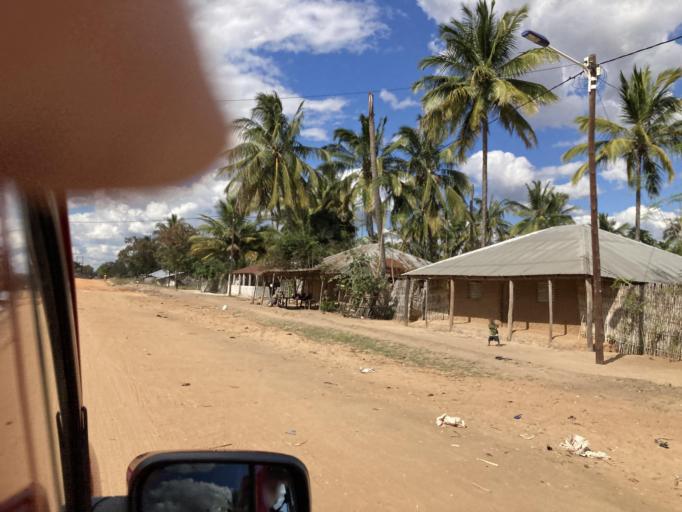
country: MZ
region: Cabo Delgado
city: Montepuez
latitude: -13.1270
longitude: 39.0190
